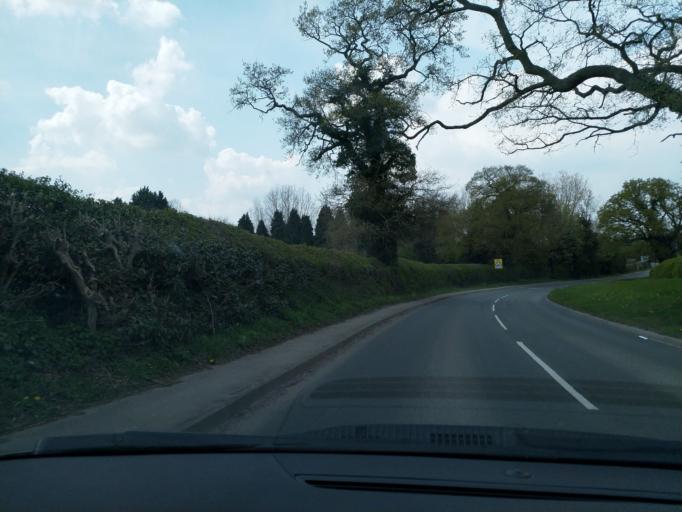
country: GB
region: England
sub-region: Warwickshire
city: Royal Leamington Spa
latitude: 52.3183
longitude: -1.5268
